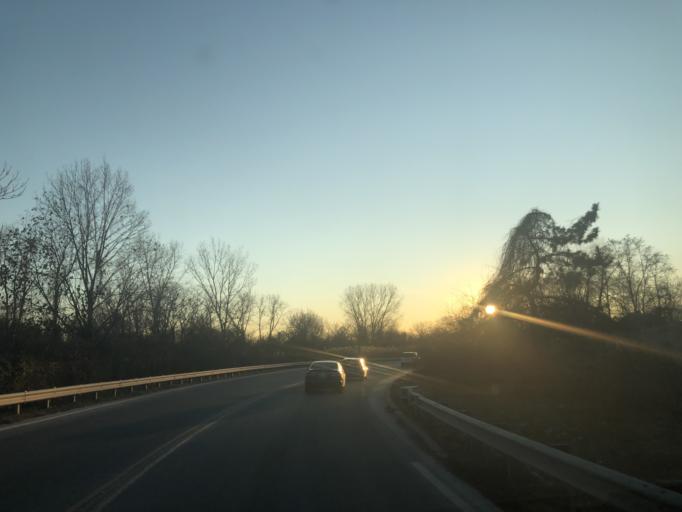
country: US
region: New Jersey
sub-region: Hudson County
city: Jersey City
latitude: 40.7082
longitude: -74.0525
